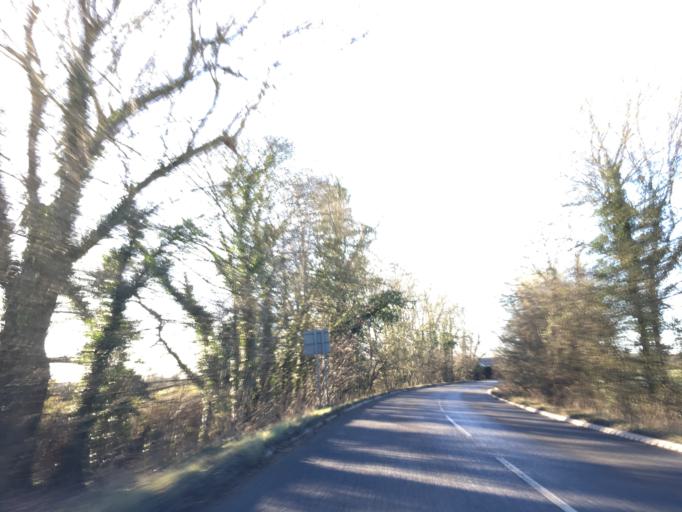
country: GB
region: England
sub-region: Wiltshire
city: Leigh
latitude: 51.6296
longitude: -1.8955
